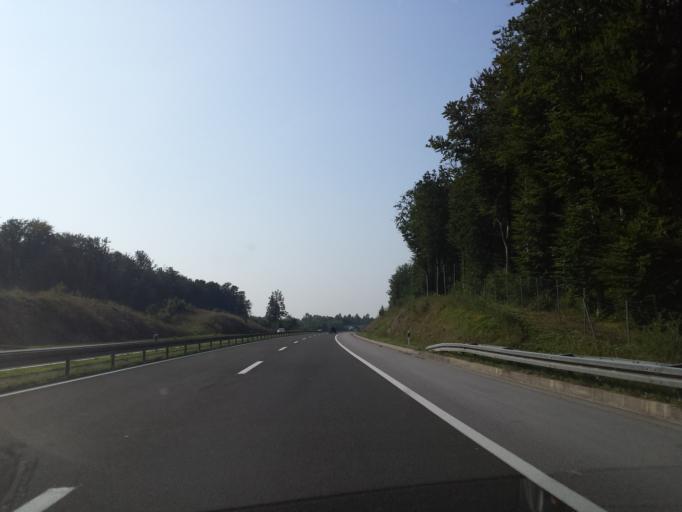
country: HR
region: Karlovacka
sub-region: Grad Ogulin
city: Ogulin
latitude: 45.3604
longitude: 15.2750
